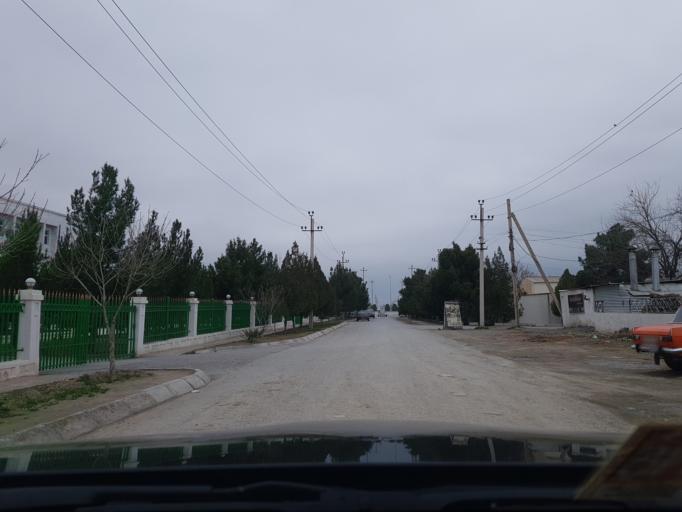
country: TM
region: Ahal
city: Abadan
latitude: 38.1618
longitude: 57.9431
